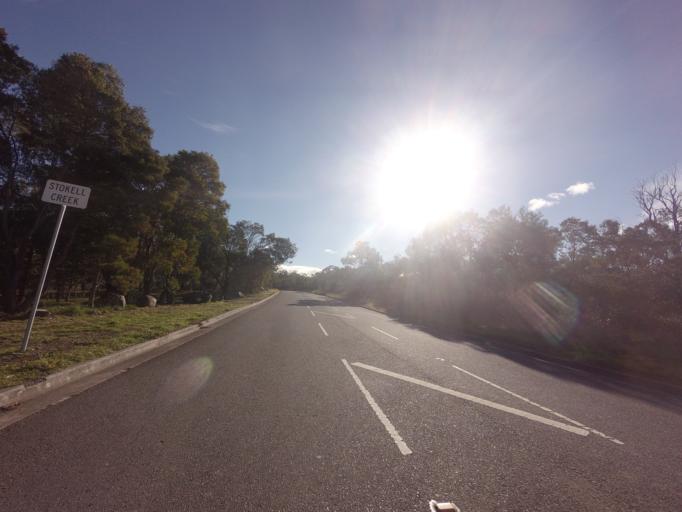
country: AU
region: Tasmania
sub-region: Clarence
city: Rokeby
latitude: -42.8884
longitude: 147.4380
